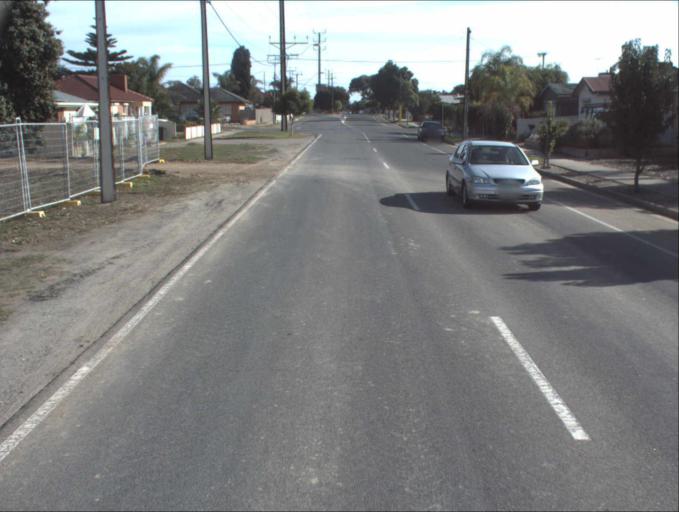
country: AU
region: South Australia
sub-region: Port Adelaide Enfield
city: Birkenhead
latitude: -34.8084
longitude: 138.4966
